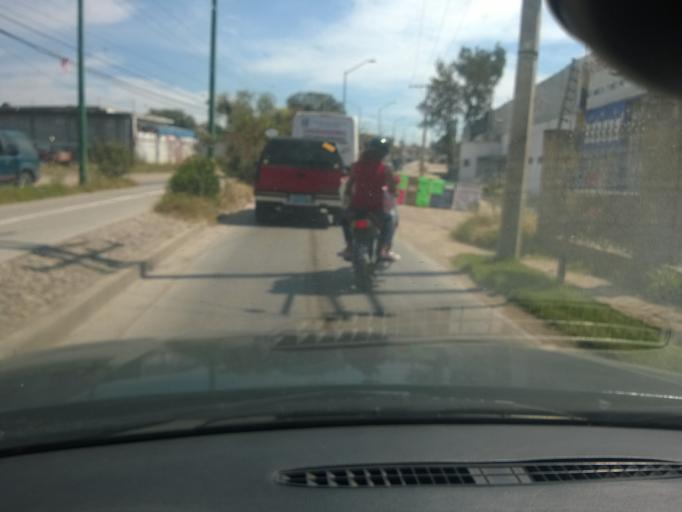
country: MX
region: Guanajuato
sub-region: Leon
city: Ejido la Joya
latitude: 21.1401
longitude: -101.7410
